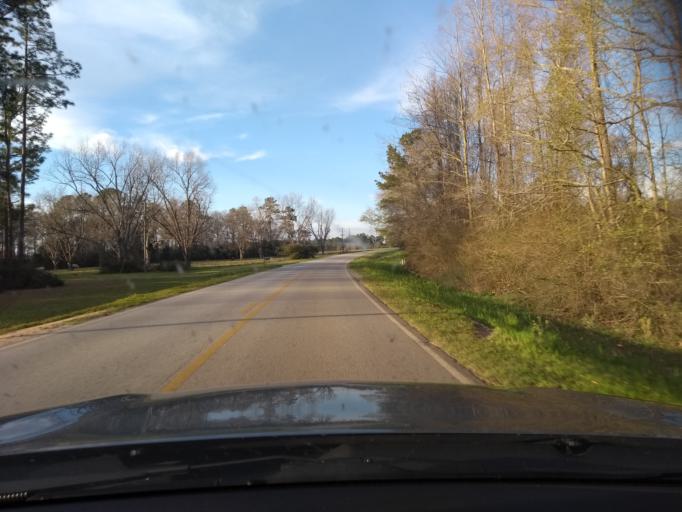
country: US
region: Georgia
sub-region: Bulloch County
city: Statesboro
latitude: 32.3420
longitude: -81.7735
